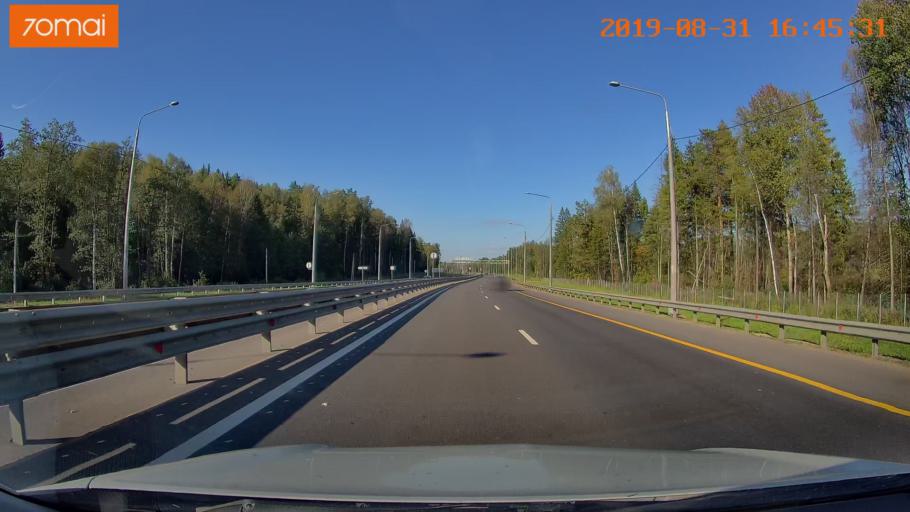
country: RU
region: Kaluga
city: Mstikhino
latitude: 54.6208
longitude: 36.1192
